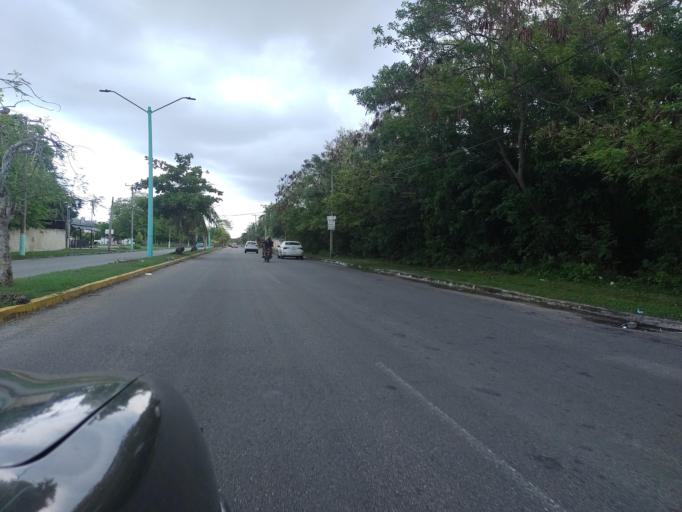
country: MX
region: Quintana Roo
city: Chetumal
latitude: 18.5108
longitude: -88.2815
